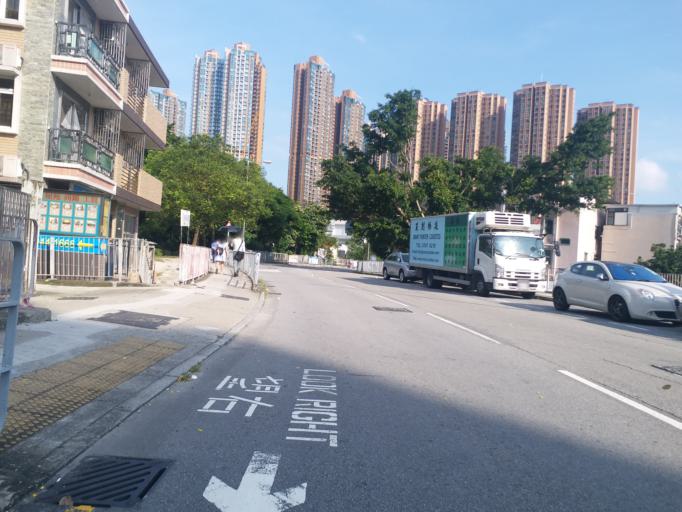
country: HK
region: Yuen Long
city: Yuen Long Kau Hui
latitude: 22.4484
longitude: 114.0337
